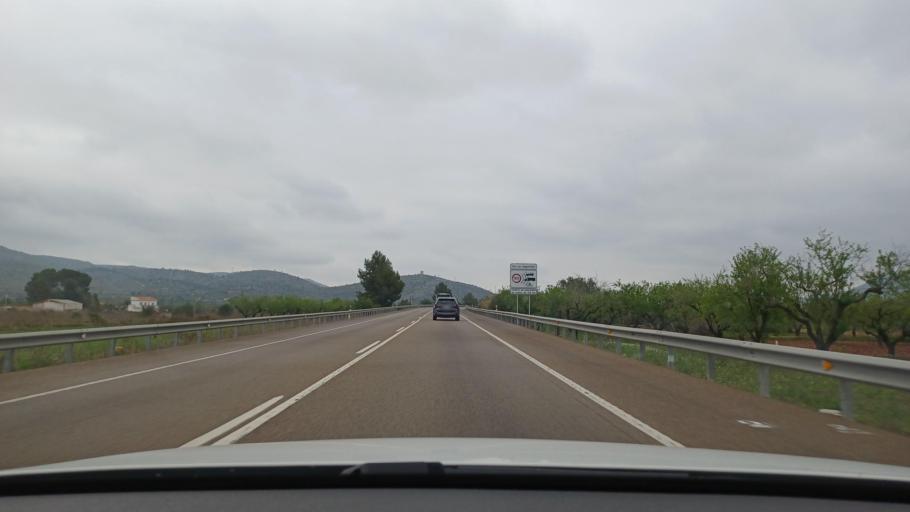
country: ES
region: Valencia
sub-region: Provincia de Castello
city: Santa Magdalena de Pulpis
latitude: 40.3570
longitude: 0.2977
